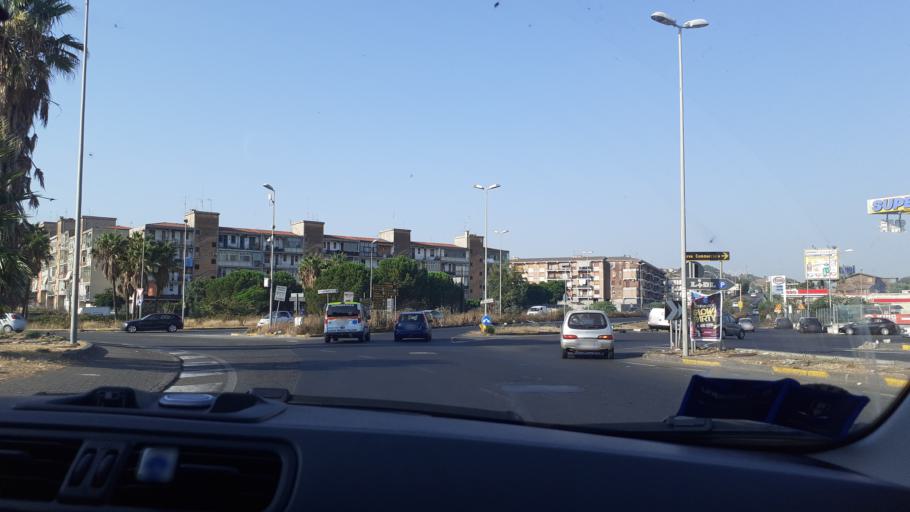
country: IT
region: Sicily
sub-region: Catania
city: Misterbianco
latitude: 37.5130
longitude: 15.0390
